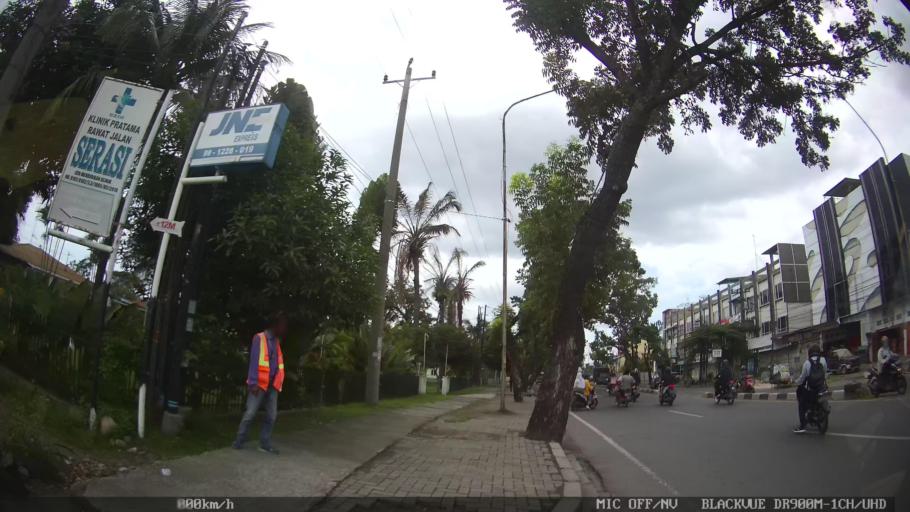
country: ID
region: North Sumatra
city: Sunggal
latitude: 3.5945
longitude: 98.6176
